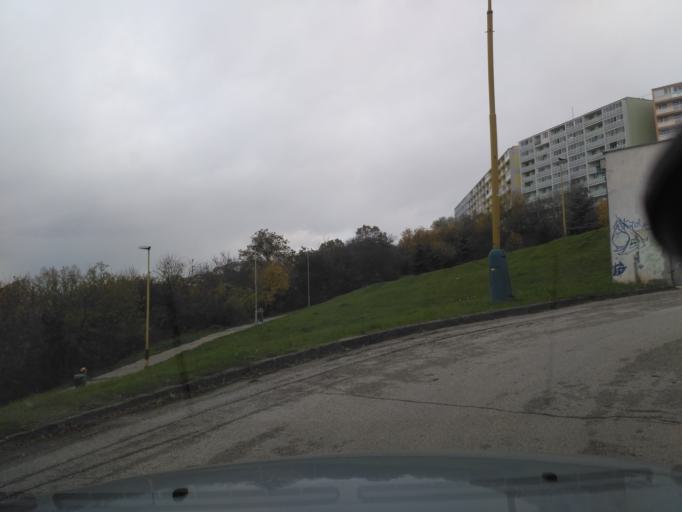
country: SK
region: Kosicky
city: Kosice
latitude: 48.7328
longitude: 21.2814
